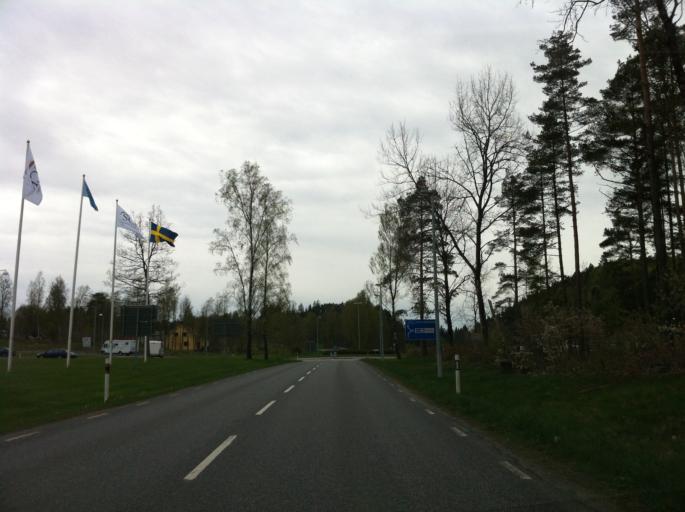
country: SE
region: Halland
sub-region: Halmstads Kommun
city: Getinge
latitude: 57.1269
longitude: 12.7141
